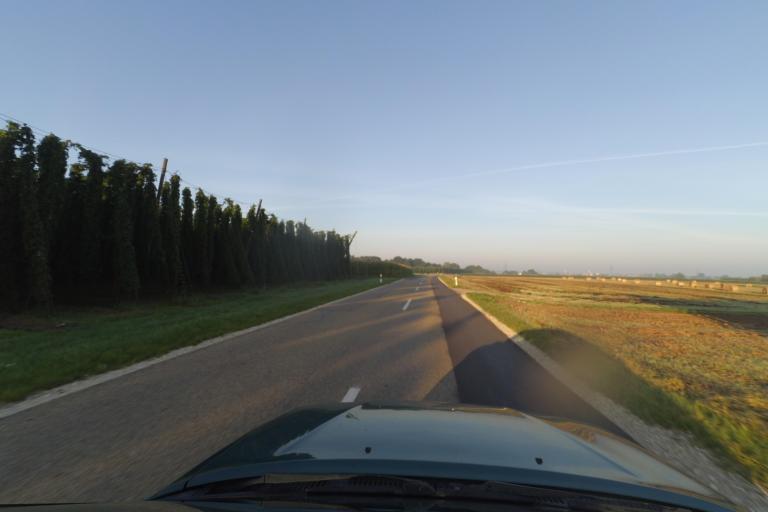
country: DE
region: Bavaria
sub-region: Upper Bavaria
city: Geisenfeld
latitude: 48.6807
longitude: 11.6481
